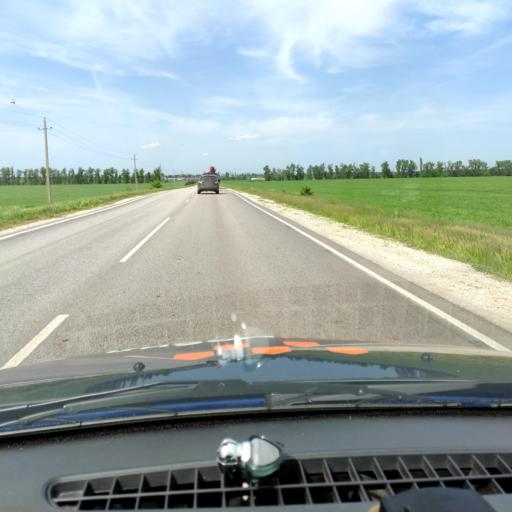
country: RU
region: Voronezj
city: Novaya Usman'
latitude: 51.5598
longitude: 39.3762
